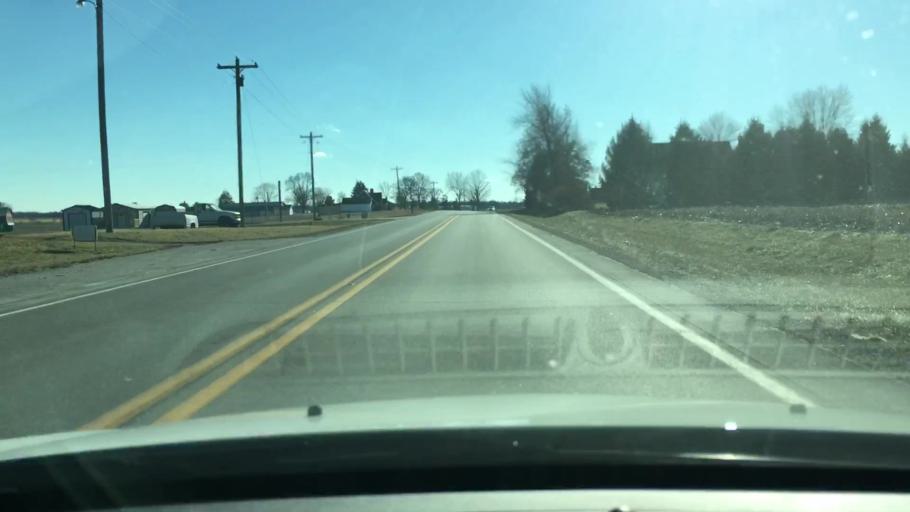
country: US
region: Illinois
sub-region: Pike County
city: Pittsfield
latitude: 39.6484
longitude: -90.7843
